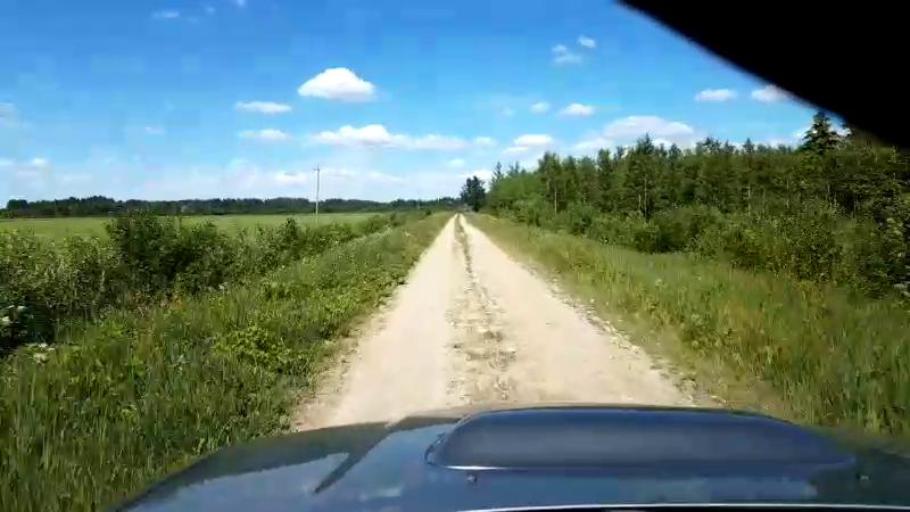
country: EE
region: Paernumaa
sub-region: Halinga vald
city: Parnu-Jaagupi
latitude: 58.5383
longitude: 24.5303
